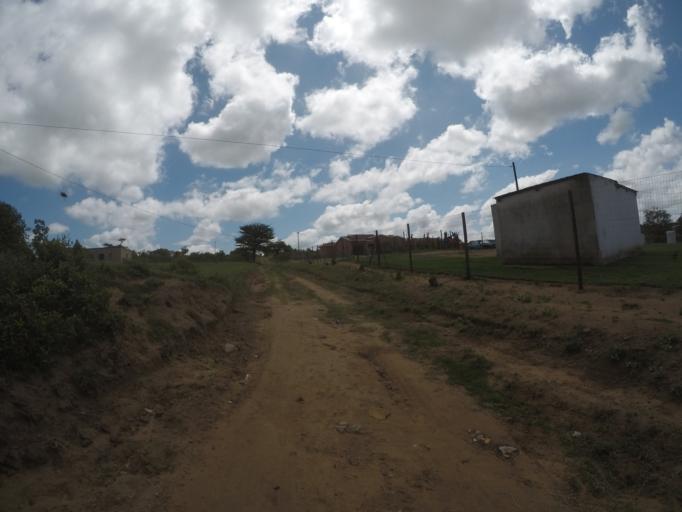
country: ZA
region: KwaZulu-Natal
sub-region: uThungulu District Municipality
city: Empangeni
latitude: -28.5865
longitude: 31.8414
